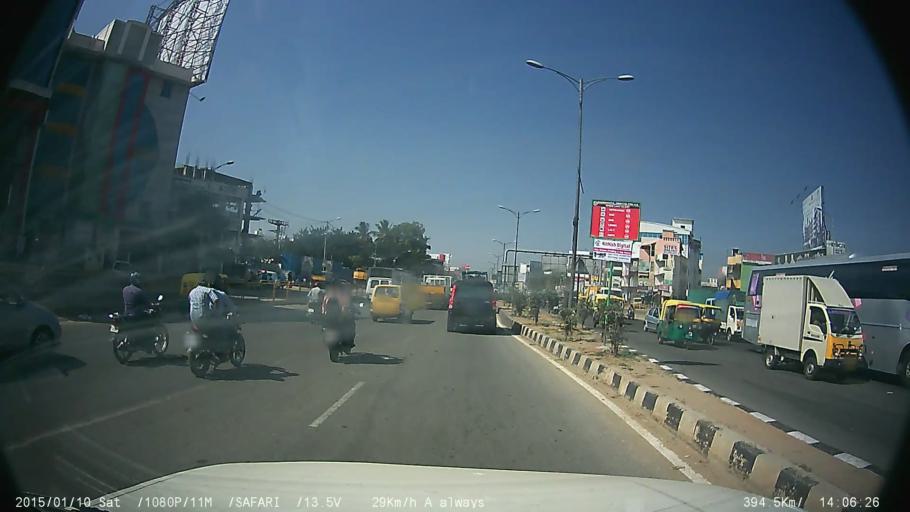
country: IN
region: Karnataka
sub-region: Bangalore Urban
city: Bangalore
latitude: 12.9093
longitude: 77.6274
